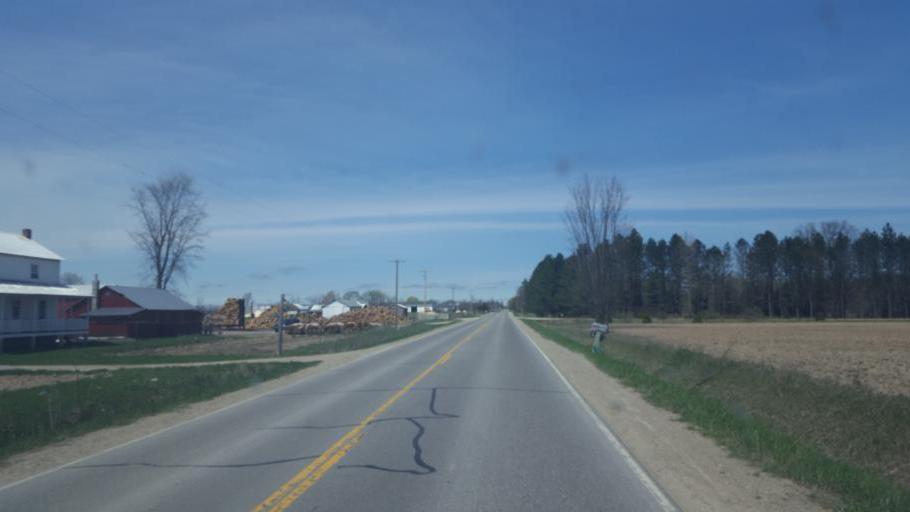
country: US
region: Michigan
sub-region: Gladwin County
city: Beaverton
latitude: 43.9292
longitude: -84.5852
